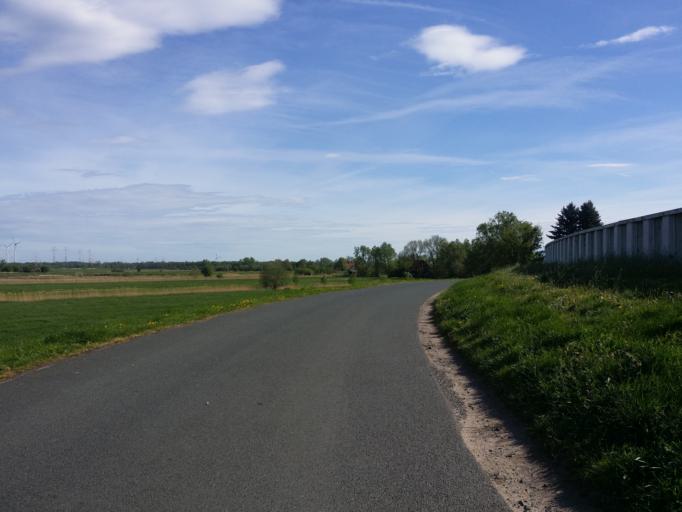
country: DE
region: Lower Saxony
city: Lemwerder
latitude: 53.1532
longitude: 8.6297
